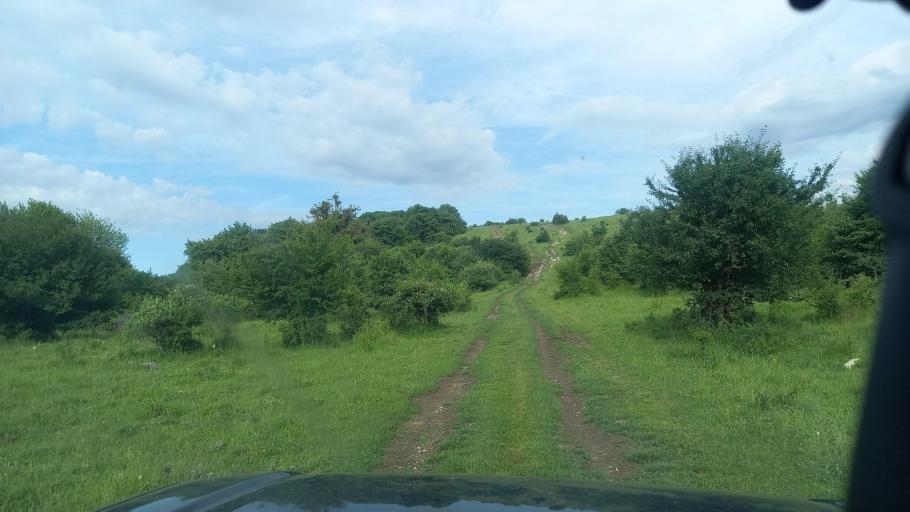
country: RU
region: Karachayevo-Cherkesiya
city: Kurdzhinovo
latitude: 44.1288
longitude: 41.0567
